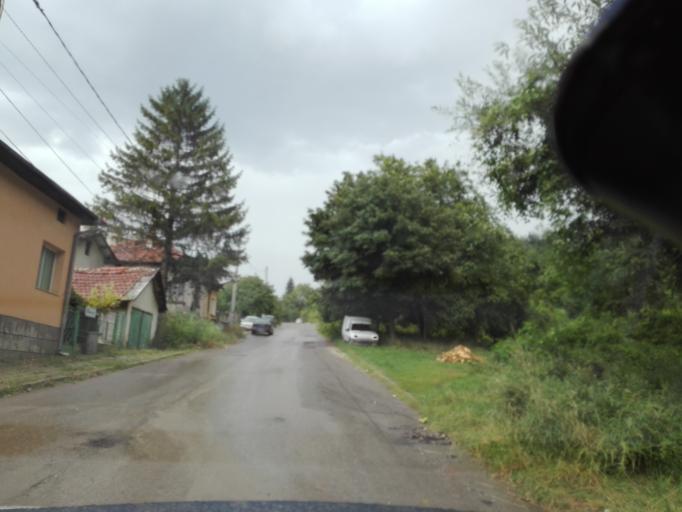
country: BG
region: Sofiya
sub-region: Obshtina Elin Pelin
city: Elin Pelin
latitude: 42.5985
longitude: 23.4808
